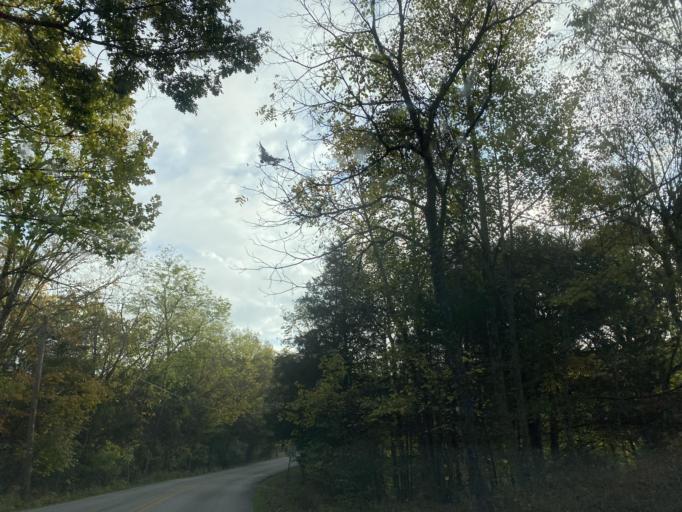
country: US
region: Kentucky
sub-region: Pendleton County
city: Falmouth
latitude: 38.7222
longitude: -84.2919
